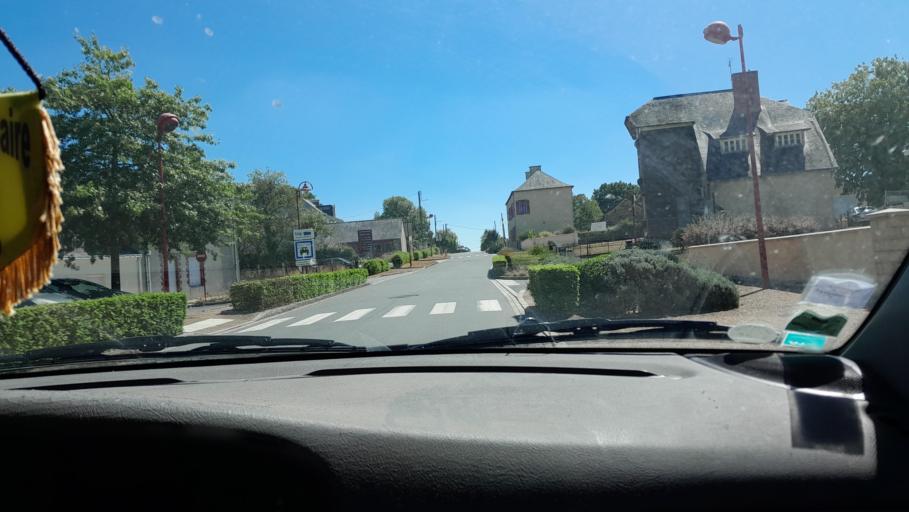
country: FR
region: Pays de la Loire
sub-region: Departement de la Loire-Atlantique
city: Saint-Mars-la-Jaille
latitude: 47.6219
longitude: -1.1983
